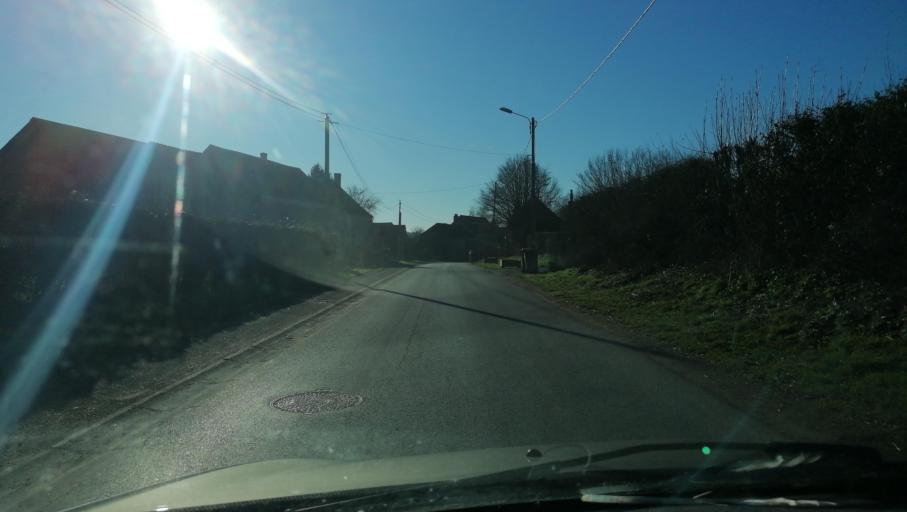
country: FR
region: Nord-Pas-de-Calais
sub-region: Departement du Nord
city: Ferriere-la-Grande
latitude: 50.2219
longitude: 4.0322
